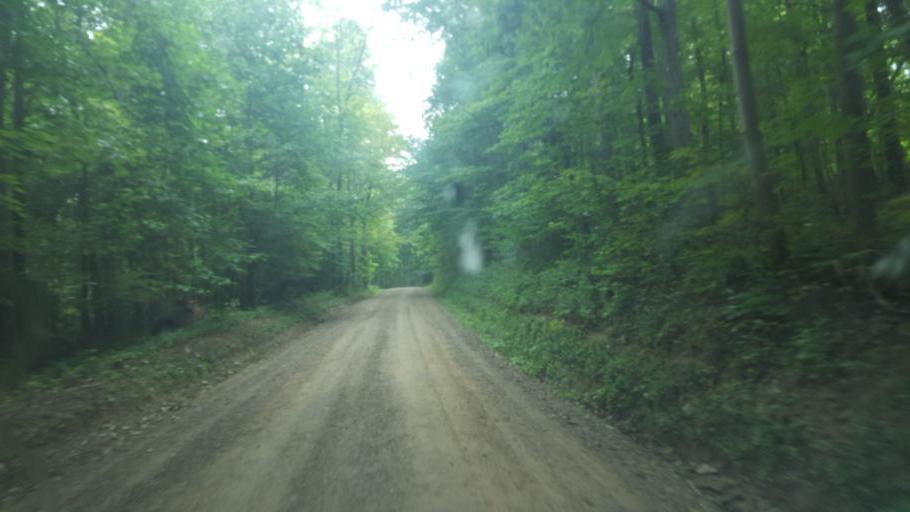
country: US
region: Ohio
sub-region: Knox County
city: Danville
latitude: 40.4804
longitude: -82.3320
